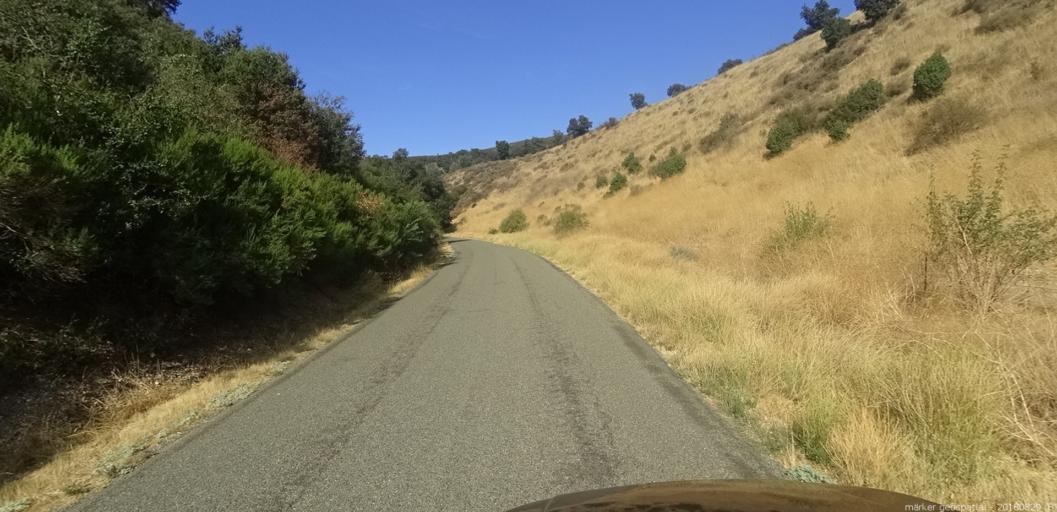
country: US
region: California
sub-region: Monterey County
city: King City
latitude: 36.0450
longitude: -121.0723
